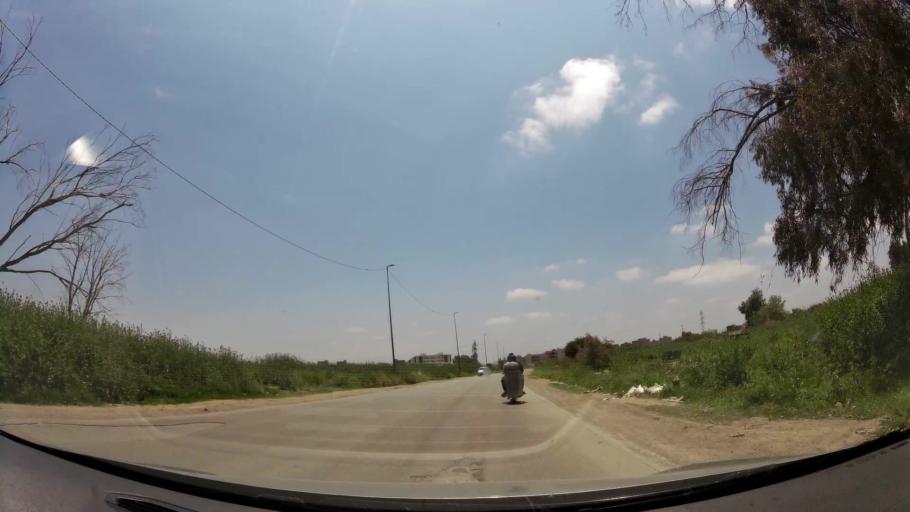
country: MA
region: Fes-Boulemane
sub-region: Fes
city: Fes
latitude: 34.0387
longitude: -5.0607
